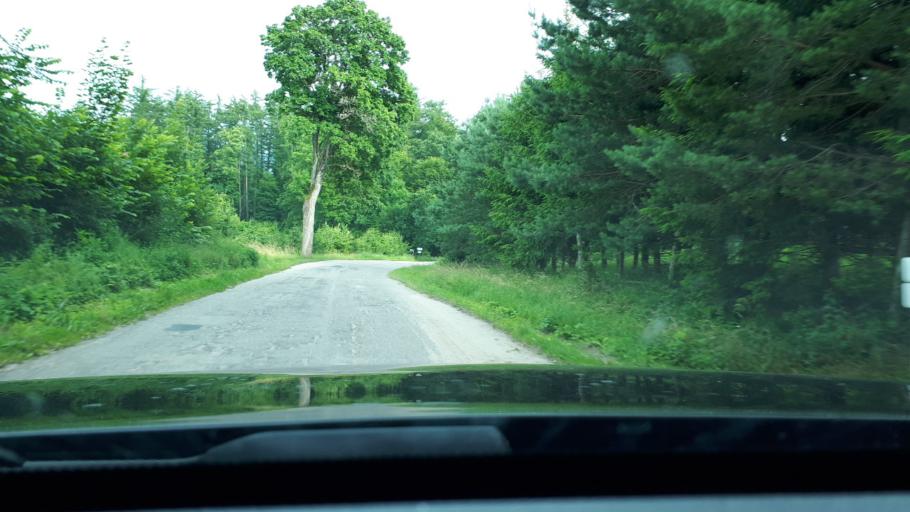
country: PL
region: Warmian-Masurian Voivodeship
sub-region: Powiat ostrodzki
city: Gierzwald
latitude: 53.6379
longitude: 20.1178
